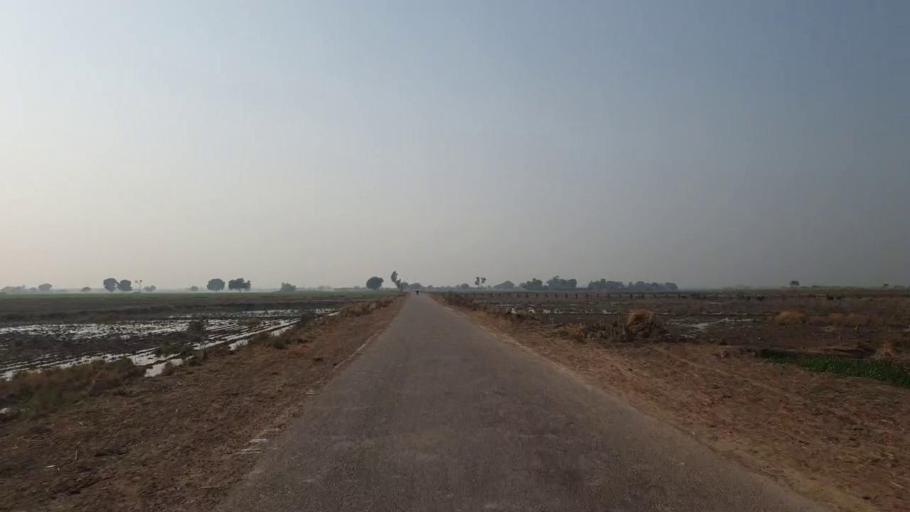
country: PK
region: Sindh
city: Shahdadpur
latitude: 25.9664
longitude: 68.5609
